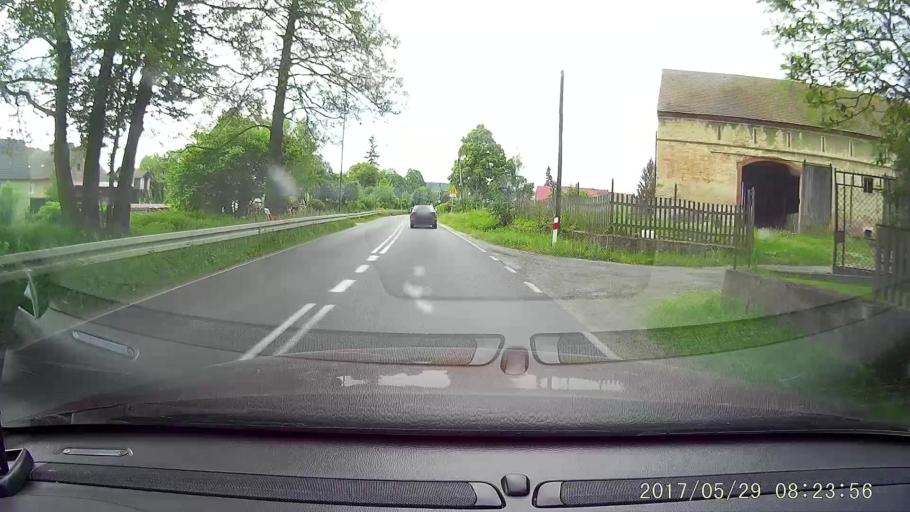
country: PL
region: Lower Silesian Voivodeship
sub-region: Powiat zlotoryjski
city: Wilkow
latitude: 51.0758
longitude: 15.8650
